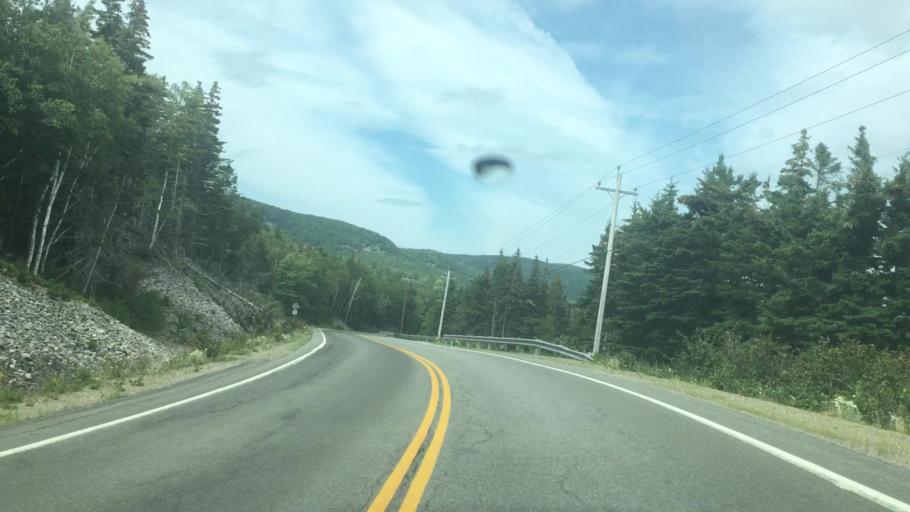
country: CA
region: Nova Scotia
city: Sydney Mines
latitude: 46.5375
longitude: -60.4134
